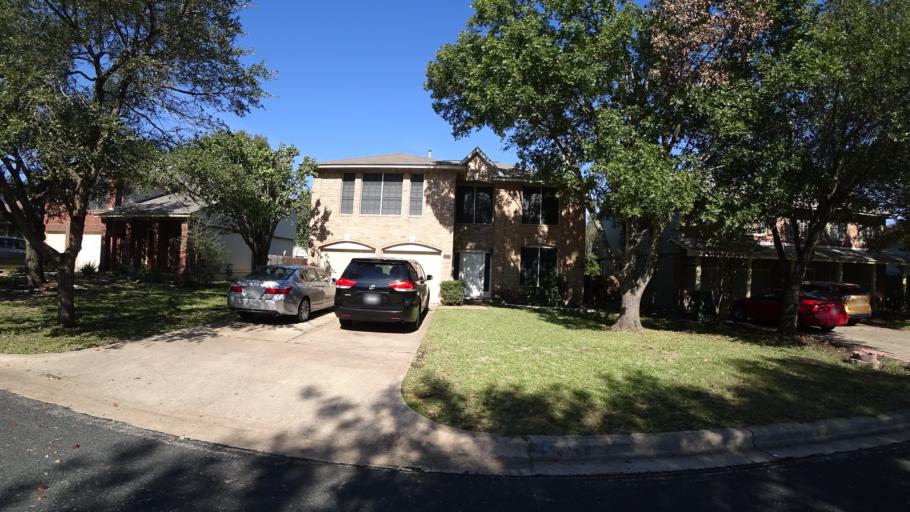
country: US
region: Texas
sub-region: Travis County
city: Shady Hollow
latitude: 30.2152
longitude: -97.8703
